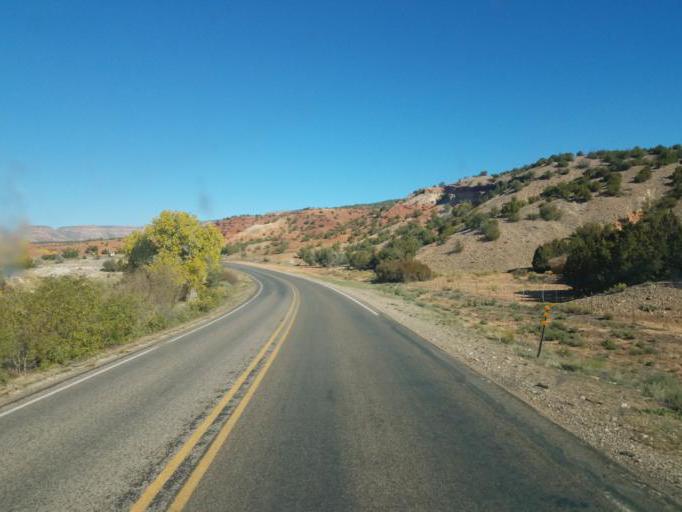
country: US
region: New Mexico
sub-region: Sandoval County
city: Jemez Pueblo
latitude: 35.6343
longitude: -106.7234
